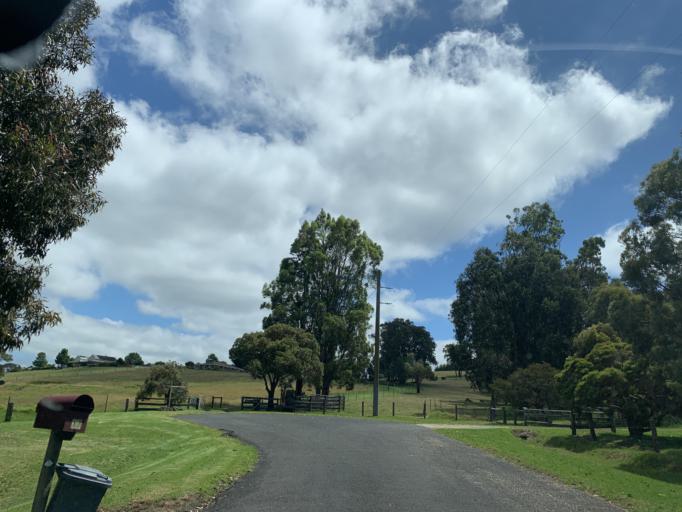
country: AU
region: Victoria
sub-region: Wellington
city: Heyfield
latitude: -38.0278
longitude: 146.6311
